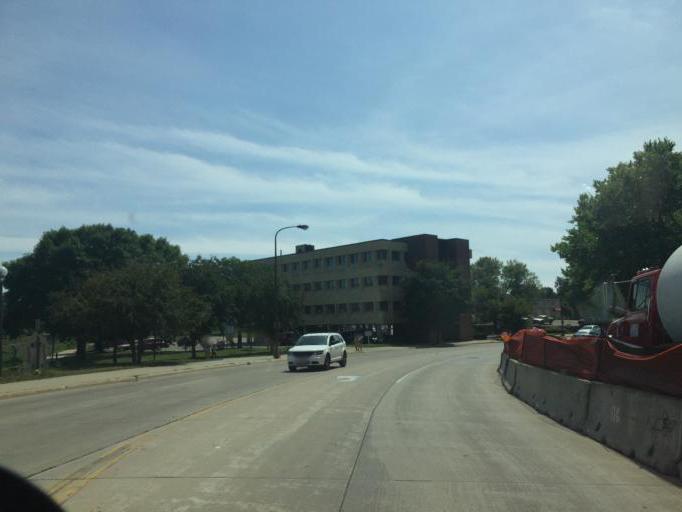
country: US
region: Minnesota
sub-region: Olmsted County
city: Rochester
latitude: 44.0208
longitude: -92.4593
